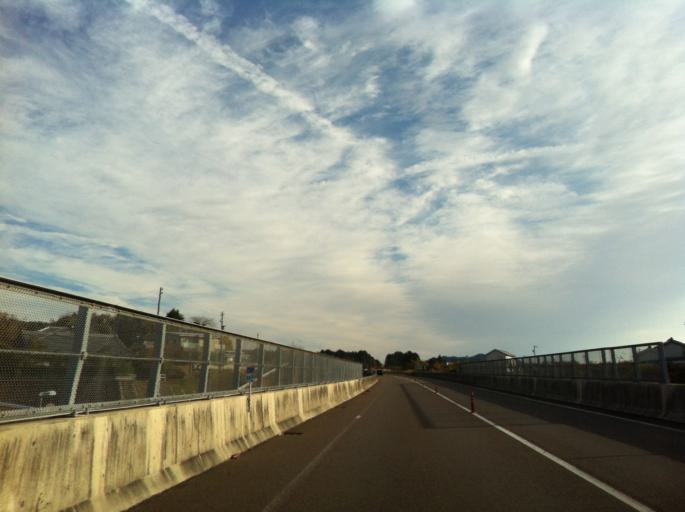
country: JP
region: Gifu
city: Minokamo
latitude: 35.4769
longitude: 137.0422
